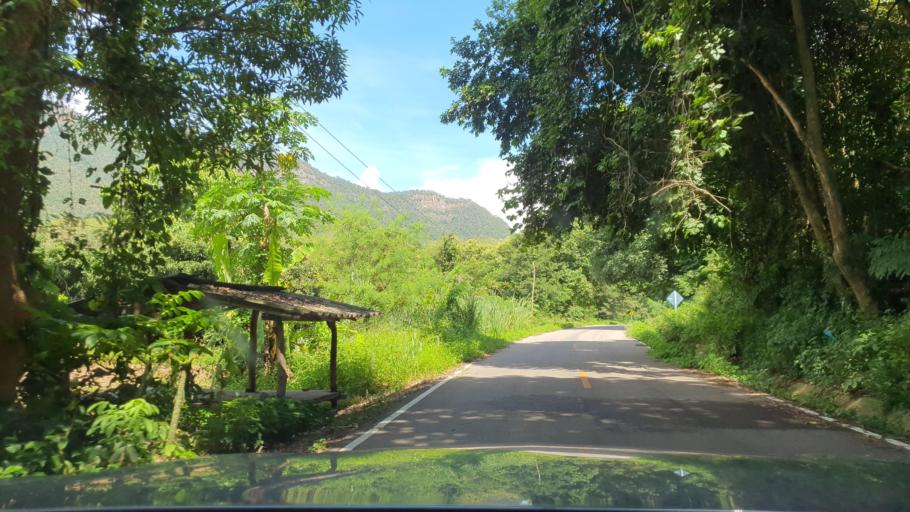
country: TH
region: Chiang Mai
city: Mae On
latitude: 18.7172
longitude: 99.2320
